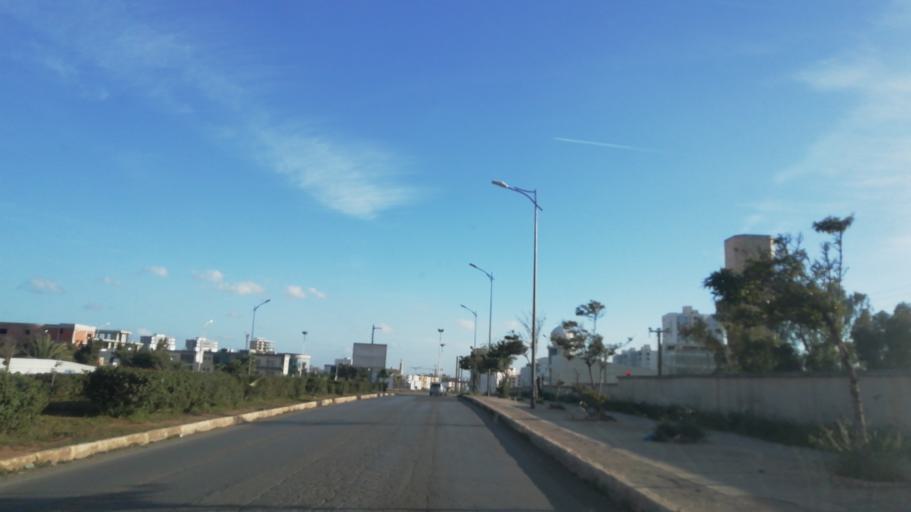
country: DZ
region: Oran
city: Bir el Djir
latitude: 35.7076
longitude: -0.5728
